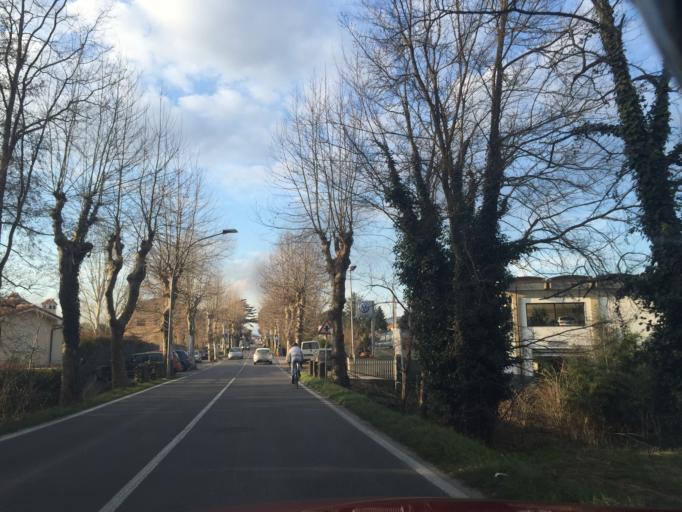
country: IT
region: Tuscany
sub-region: Provincia di Pistoia
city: Lamporecchio
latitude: 43.8195
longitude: 10.8828
